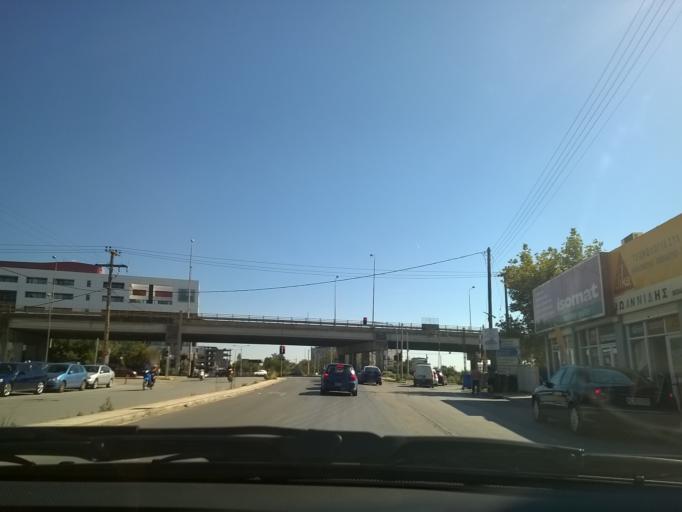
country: GR
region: Central Macedonia
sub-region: Nomos Thessalonikis
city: Menemeni
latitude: 40.6573
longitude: 22.9026
